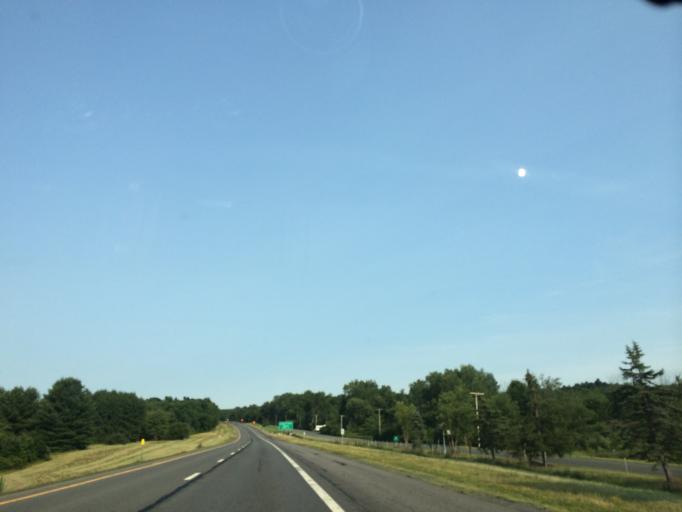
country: US
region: New York
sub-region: Rensselaer County
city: Castleton-on-Hudson
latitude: 42.4885
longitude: -73.7061
